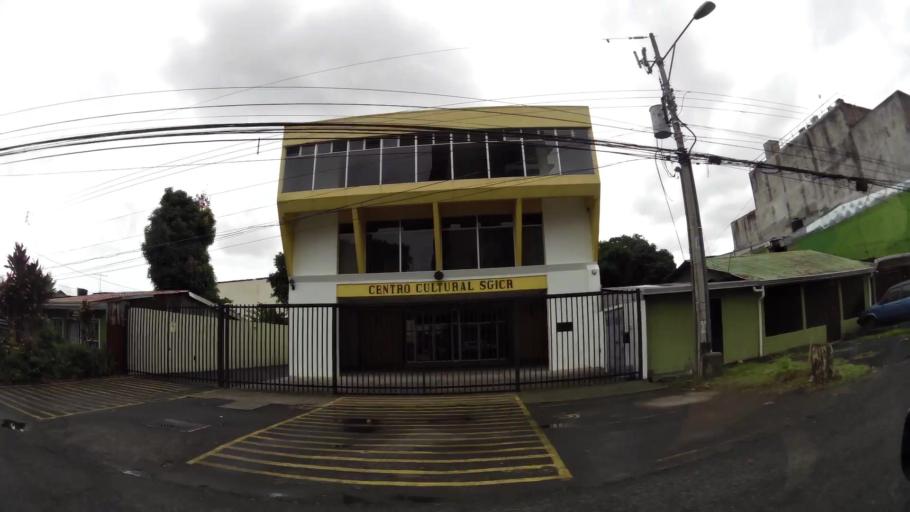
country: CR
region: San Jose
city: San Jose
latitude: 9.9388
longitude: -84.1021
